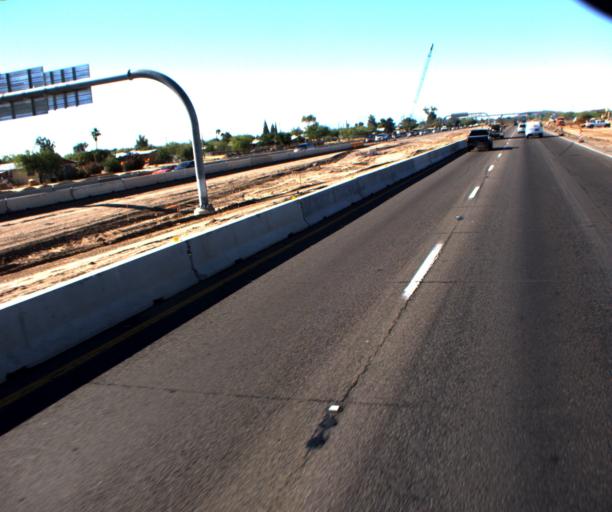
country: US
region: Arizona
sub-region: Pima County
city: South Tucson
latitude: 32.1741
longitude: -110.9858
